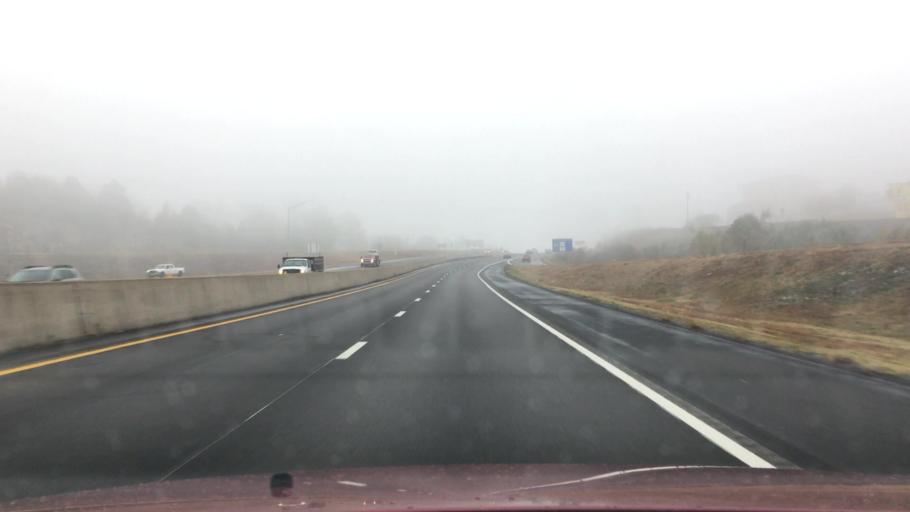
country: US
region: Missouri
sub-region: Taney County
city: Branson
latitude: 36.6679
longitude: -93.2214
